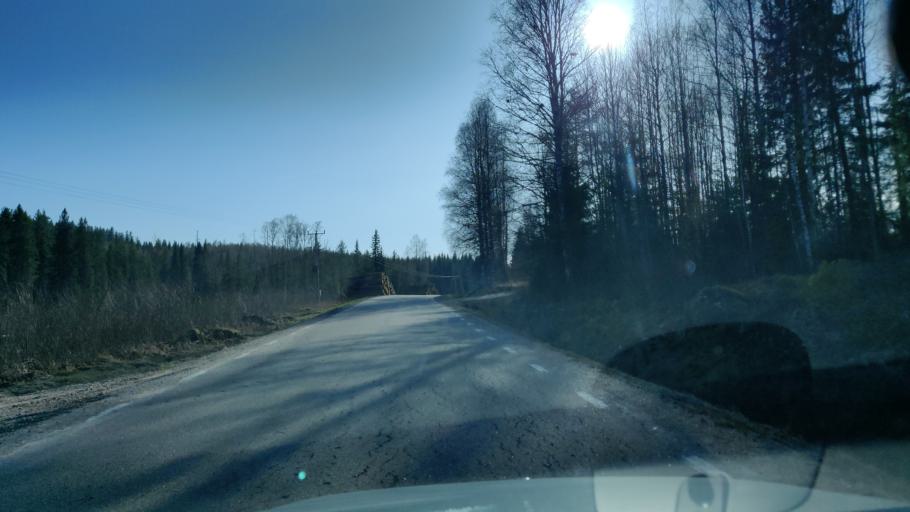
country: SE
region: Vaermland
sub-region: Munkfors Kommun
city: Munkfors
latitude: 59.9847
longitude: 13.3839
